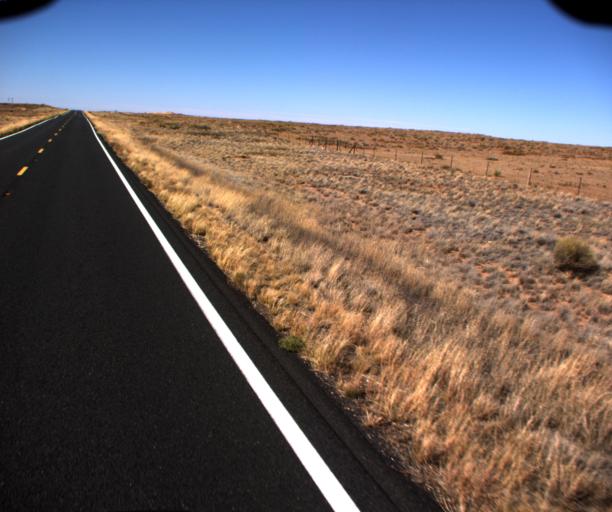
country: US
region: Arizona
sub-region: Coconino County
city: Tuba City
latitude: 35.9910
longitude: -111.0132
